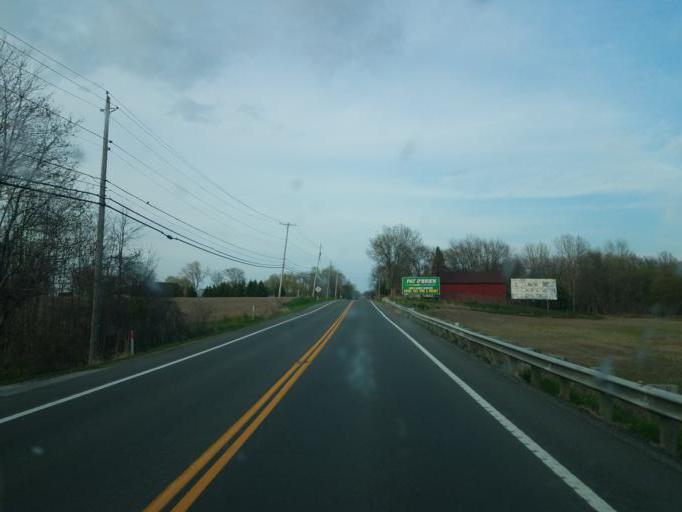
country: US
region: Ohio
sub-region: Lorain County
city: Vermilion
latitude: 41.4079
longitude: -82.4052
